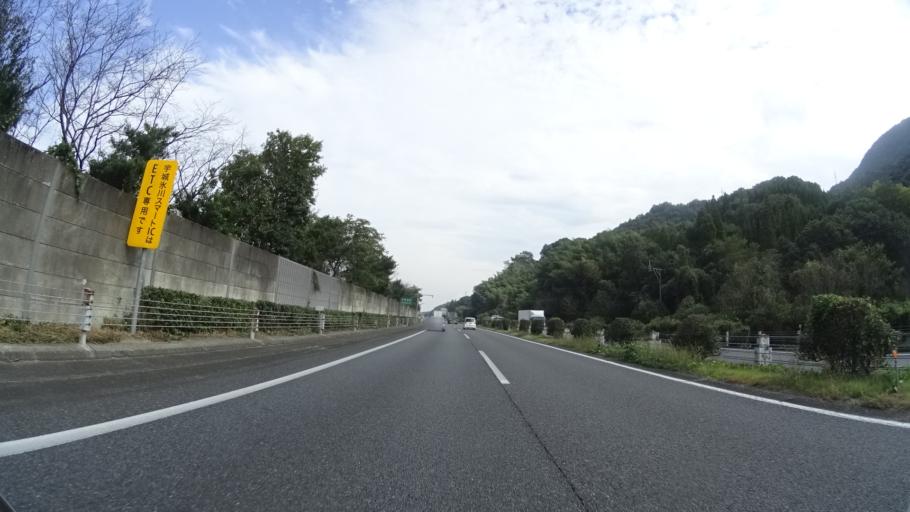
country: JP
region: Kumamoto
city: Yatsushiro
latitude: 32.5231
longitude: 130.6597
